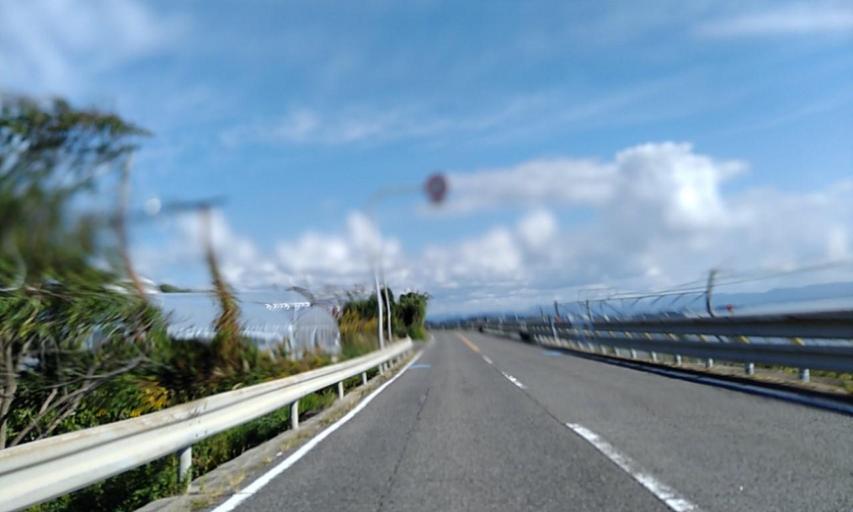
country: JP
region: Wakayama
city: Tanabe
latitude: 33.7831
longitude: 135.2603
